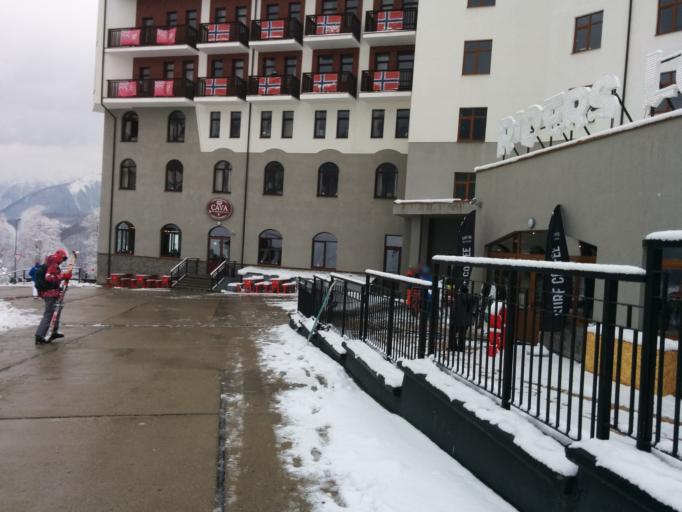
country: RU
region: Krasnodarskiy
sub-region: Sochi City
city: Krasnaya Polyana
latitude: 43.6606
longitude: 40.3201
